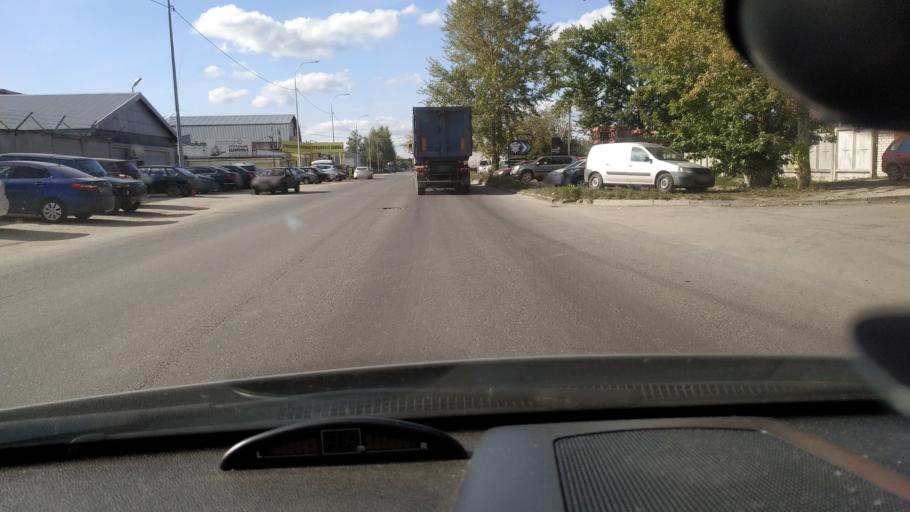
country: RU
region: Rjazan
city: Ryazan'
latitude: 54.6547
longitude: 39.6397
